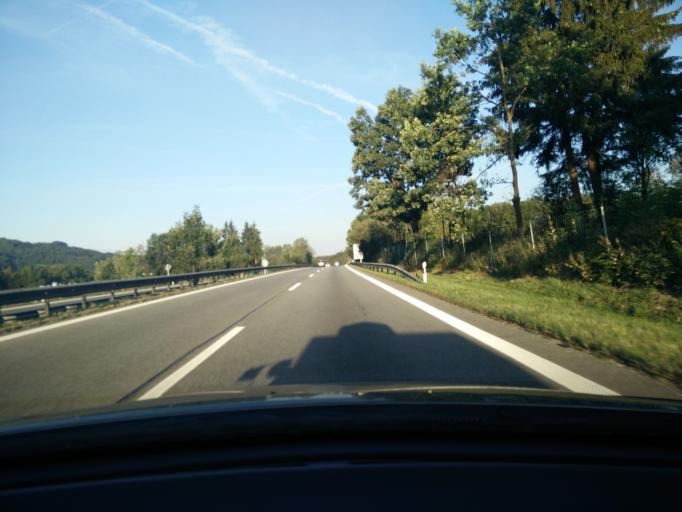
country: DE
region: Bavaria
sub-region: Upper Bavaria
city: Frasdorf
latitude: 47.7981
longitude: 12.2442
